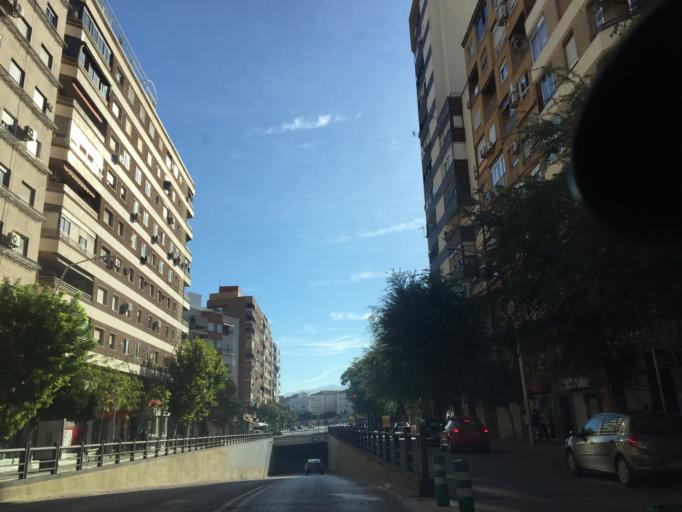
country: ES
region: Andalusia
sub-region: Provincia de Jaen
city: Jaen
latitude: 37.7772
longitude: -3.7924
